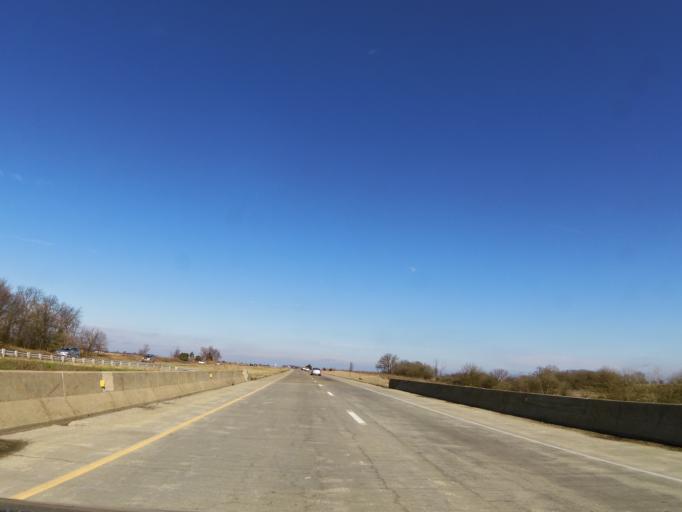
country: US
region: Illinois
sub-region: LaSalle County
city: La Salle
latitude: 41.4191
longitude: -89.0586
